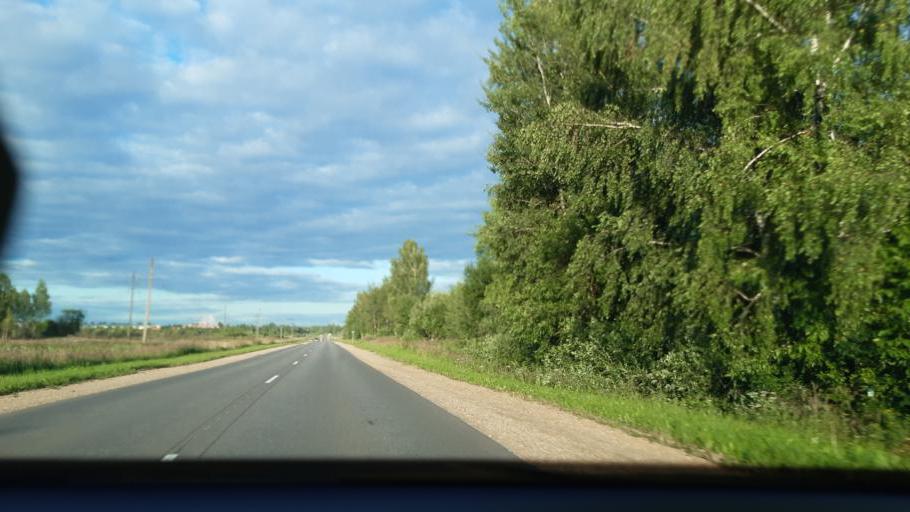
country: RU
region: Smolensk
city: Yel'nya
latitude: 54.5932
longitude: 33.1679
